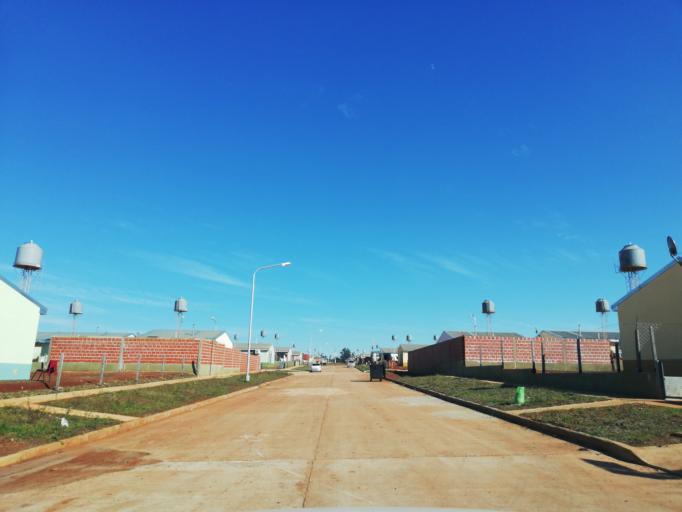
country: AR
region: Misiones
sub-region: Departamento de Capital
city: Posadas
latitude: -27.4119
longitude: -55.9899
